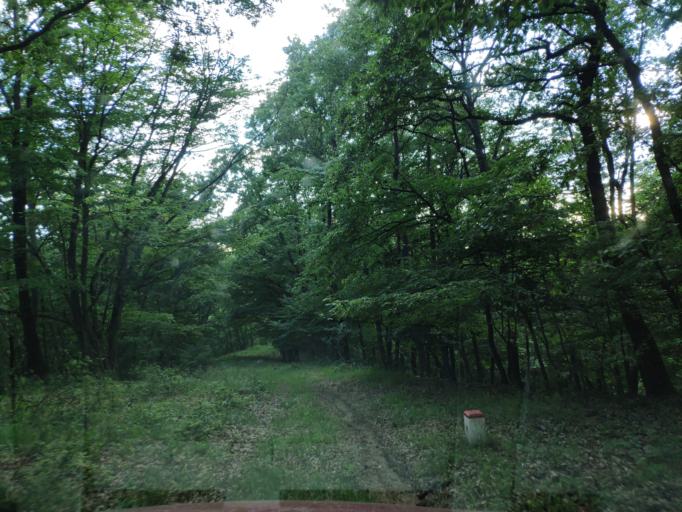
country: HU
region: Borsod-Abauj-Zemplen
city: Arlo
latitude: 48.2544
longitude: 20.1353
